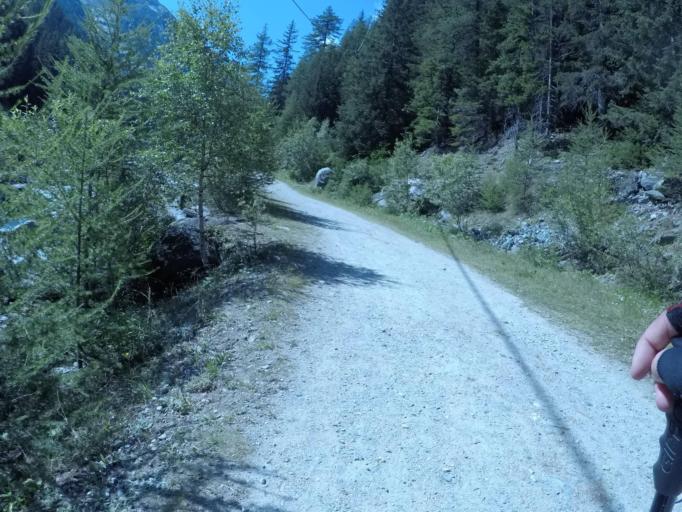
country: IT
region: Aosta Valley
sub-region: Valle d'Aosta
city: Cogne
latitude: 45.5945
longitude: 7.3472
